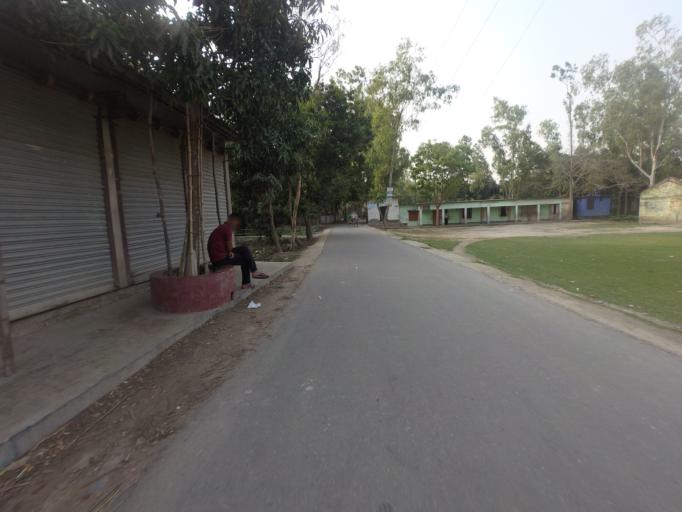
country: BD
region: Rajshahi
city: Sirajganj
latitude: 24.3191
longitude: 89.6949
